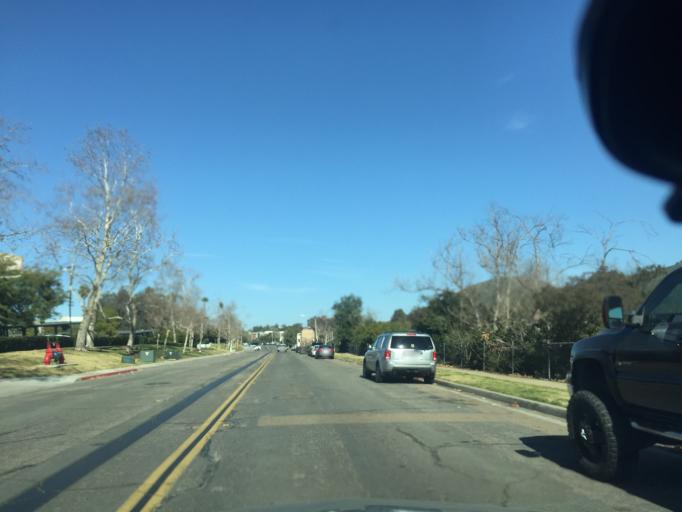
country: US
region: California
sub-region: San Diego County
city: Poway
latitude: 32.9573
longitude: -117.0971
